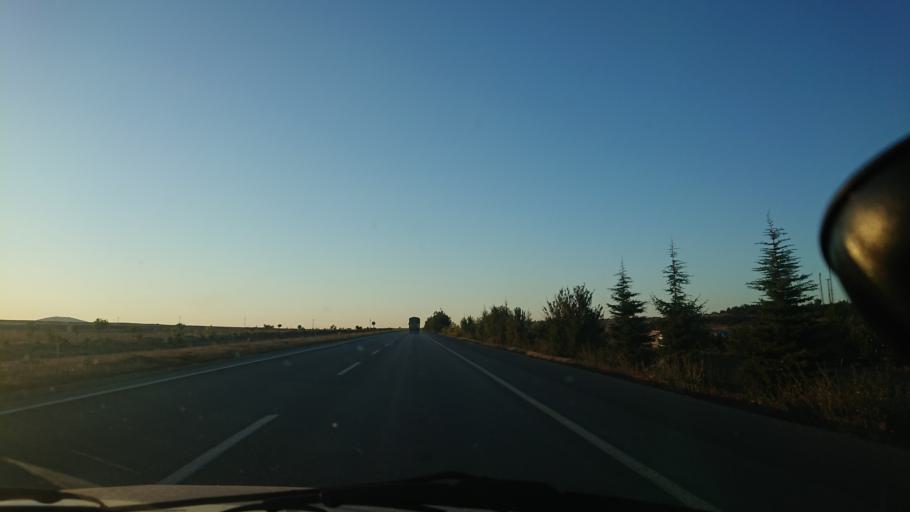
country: TR
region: Eskisehir
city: Mahmudiye
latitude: 39.4923
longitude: 30.9766
